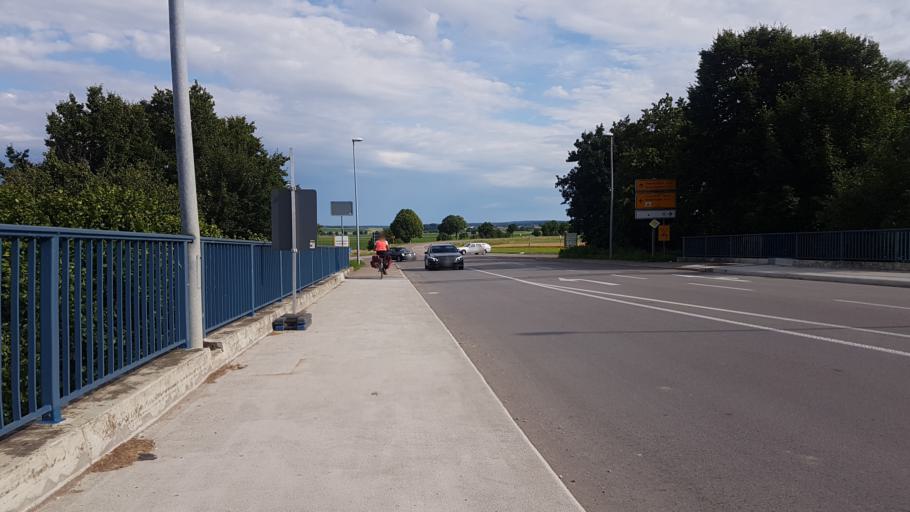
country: DE
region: Baden-Wuerttemberg
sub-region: Tuebingen Region
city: Rottenacker
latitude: 48.2311
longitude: 9.6897
